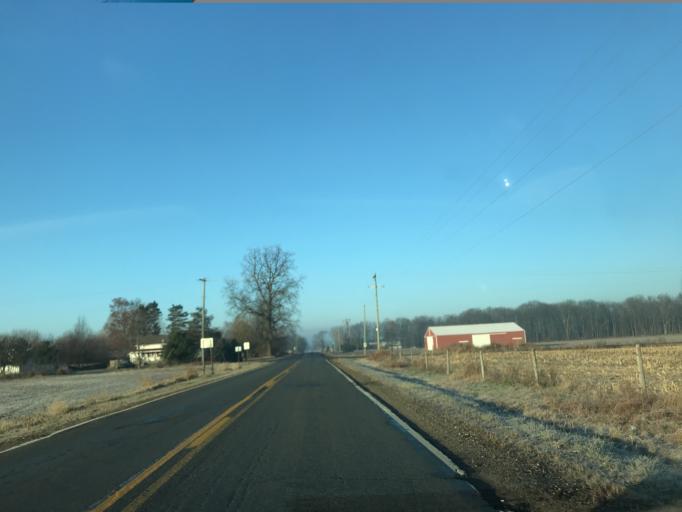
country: US
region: Michigan
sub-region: Eaton County
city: Eaton Rapids
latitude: 42.4511
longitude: -84.5994
